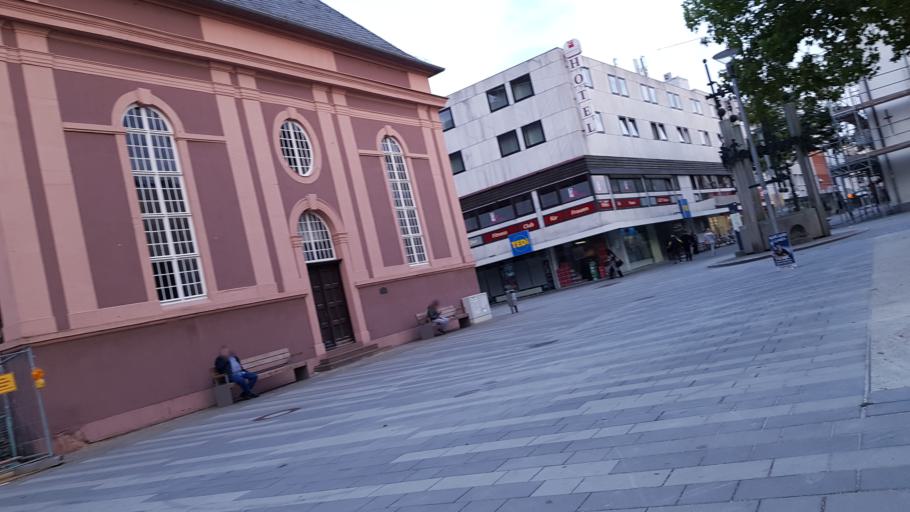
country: DE
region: Hesse
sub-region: Regierungsbezirk Darmstadt
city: Russelsheim
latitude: 49.9950
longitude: 8.4119
